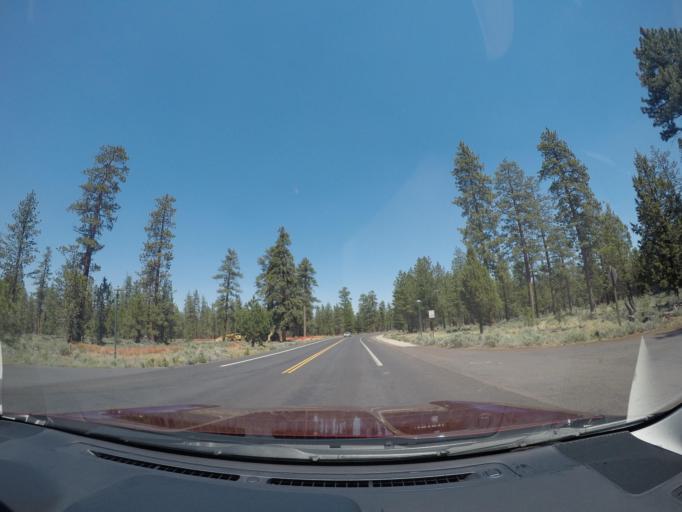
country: US
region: Oregon
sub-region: Deschutes County
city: Sisters
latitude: 44.2963
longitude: -121.5581
